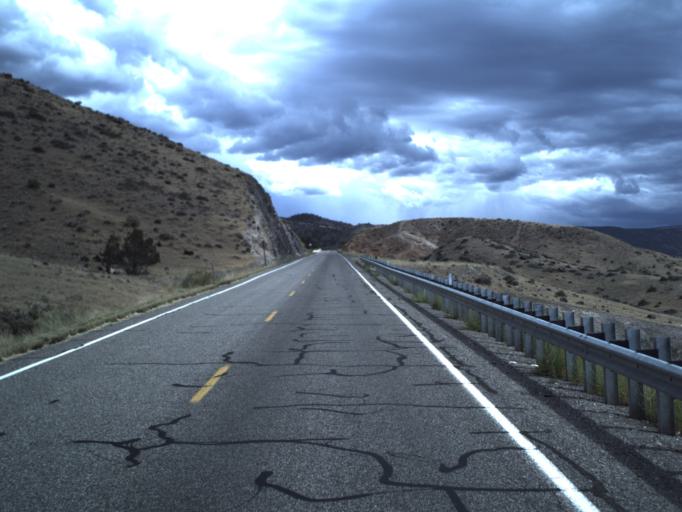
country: US
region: Utah
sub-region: Sevier County
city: Richfield
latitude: 38.7720
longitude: -111.9834
